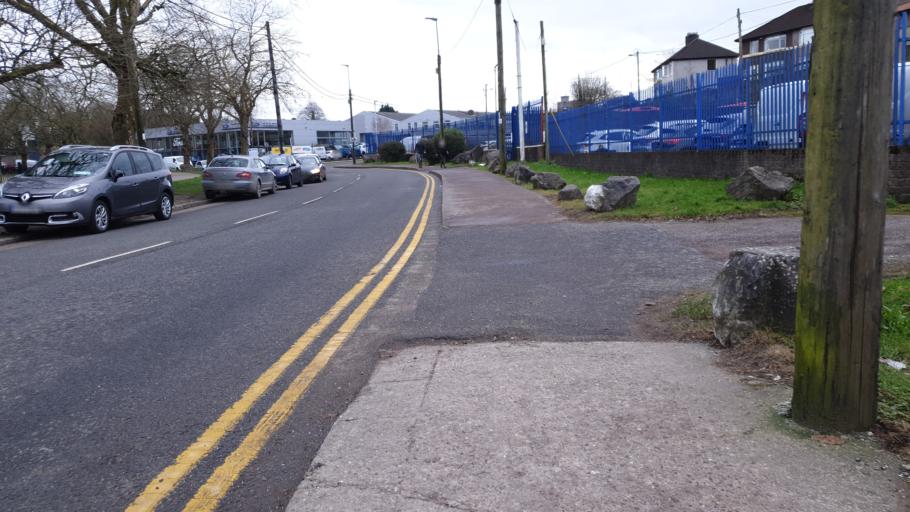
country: IE
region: Munster
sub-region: County Cork
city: Cork
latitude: 51.8976
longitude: -8.4359
